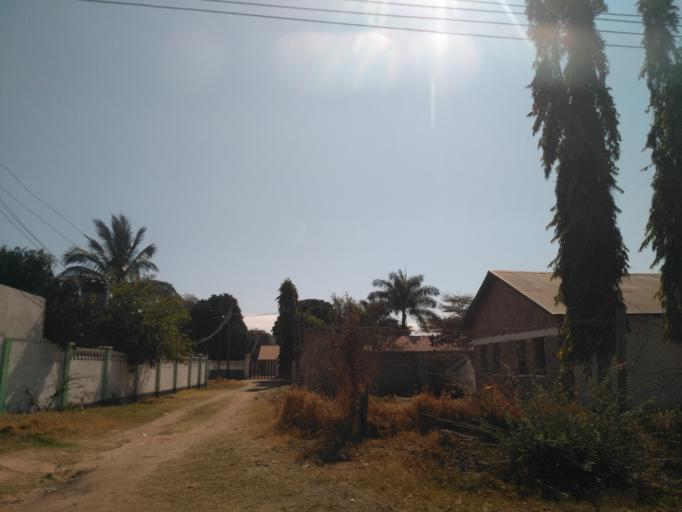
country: TZ
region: Dodoma
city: Dodoma
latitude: -6.1615
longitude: 35.7510
